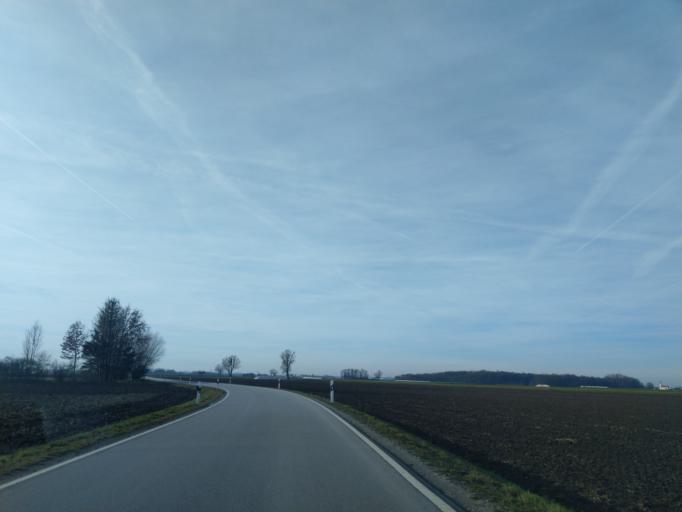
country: DE
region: Bavaria
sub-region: Lower Bavaria
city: Otzing
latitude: 48.7377
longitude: 12.8010
